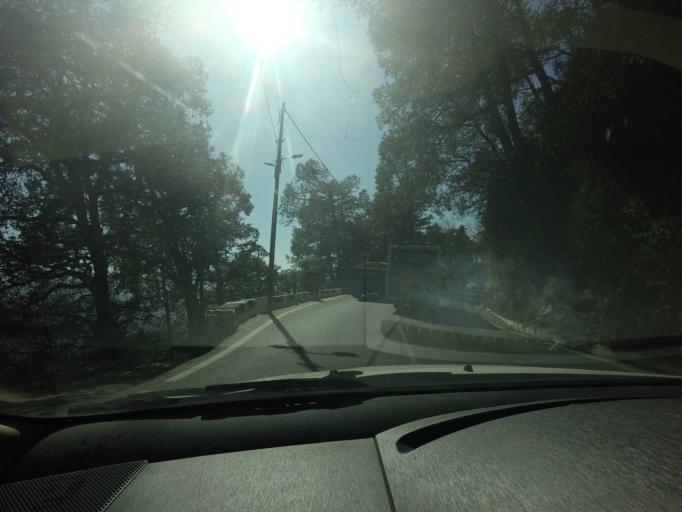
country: IN
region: Himachal Pradesh
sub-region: Shimla
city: Shimla
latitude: 31.1021
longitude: 77.1526
